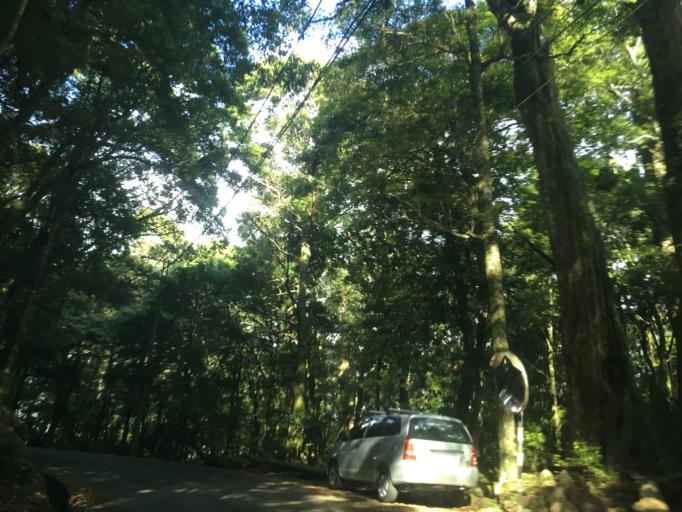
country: TW
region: Taiwan
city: Fengyuan
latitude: 24.2264
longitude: 120.9754
